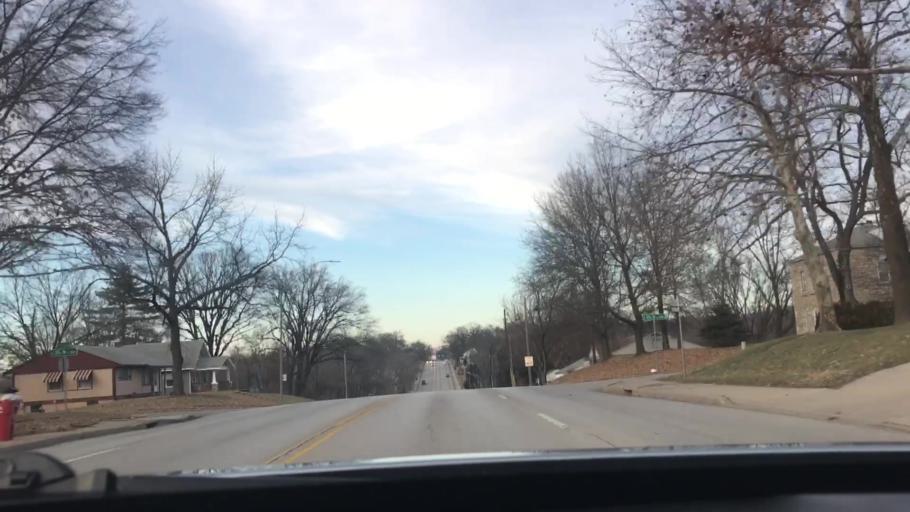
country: US
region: Missouri
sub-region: Jackson County
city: Independence
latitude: 39.0728
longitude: -94.4464
